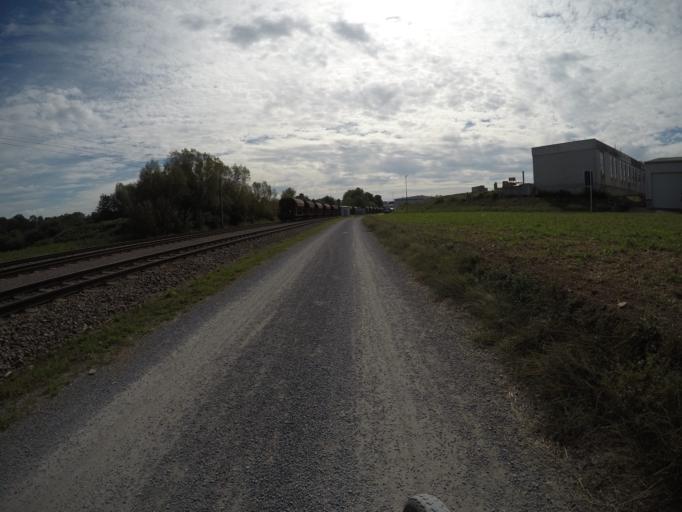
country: DE
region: Baden-Wuerttemberg
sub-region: Karlsruhe Region
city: Zaisenhausen
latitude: 49.1138
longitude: 8.7399
